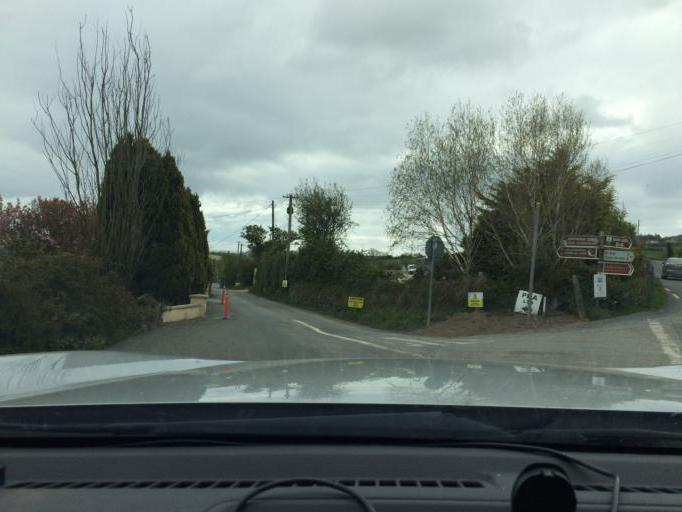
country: IE
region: Munster
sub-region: Waterford
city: Dungarvan
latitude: 52.0549
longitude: -7.6306
